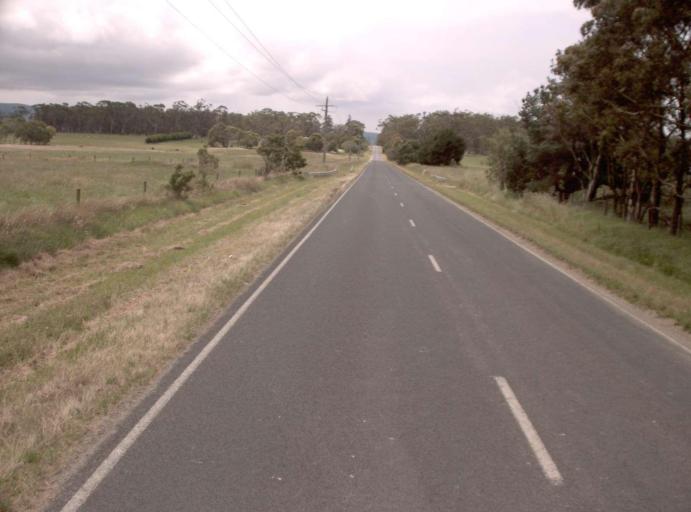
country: AU
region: Victoria
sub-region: Latrobe
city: Traralgon
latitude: -38.5485
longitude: 146.6550
